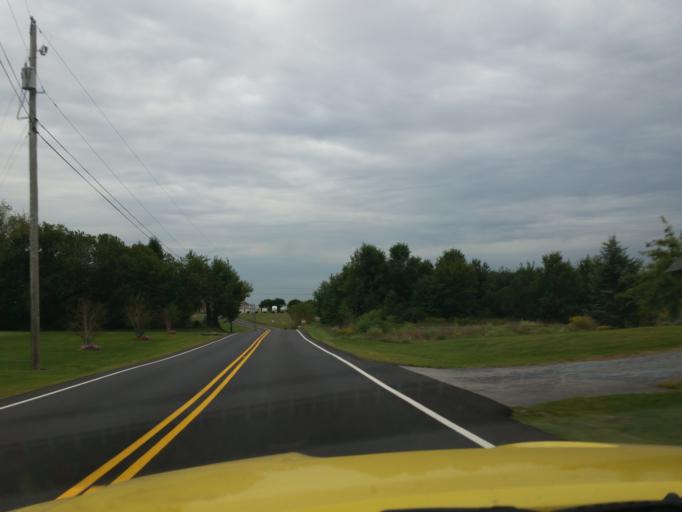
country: US
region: Pennsylvania
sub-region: Lebanon County
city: Fredericksburg
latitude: 40.4527
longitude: -76.3776
